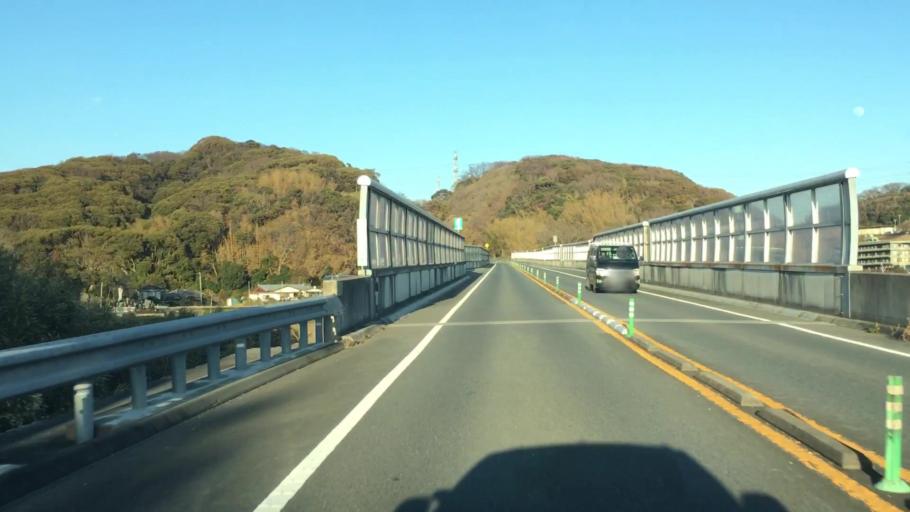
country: JP
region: Kanagawa
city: Yokosuka
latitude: 35.2312
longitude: 139.6466
